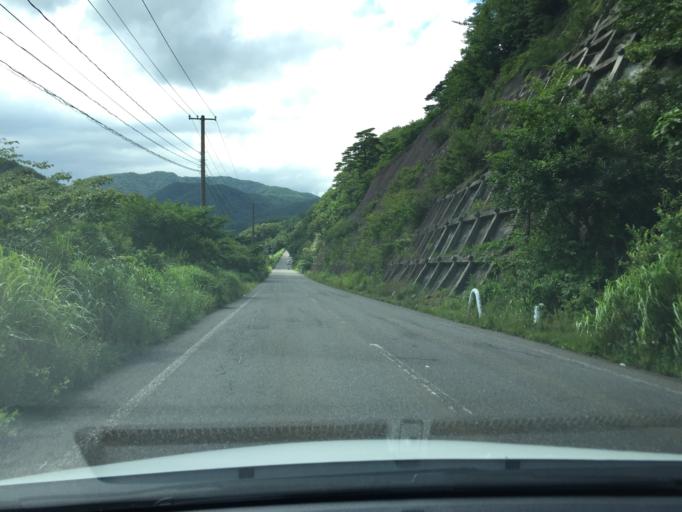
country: JP
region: Fukushima
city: Inawashiro
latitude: 37.2739
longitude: 140.0737
